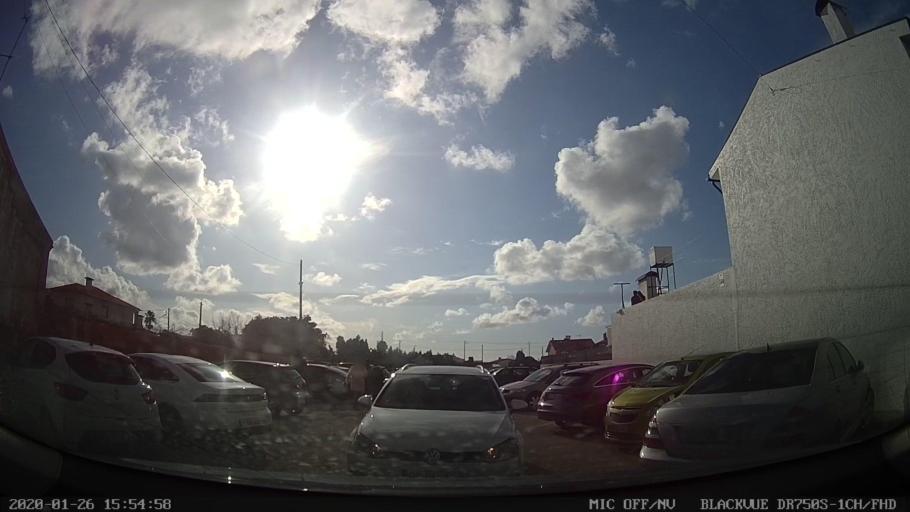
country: PT
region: Aveiro
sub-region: Aveiro
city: Aradas
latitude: 40.6278
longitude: -8.6271
